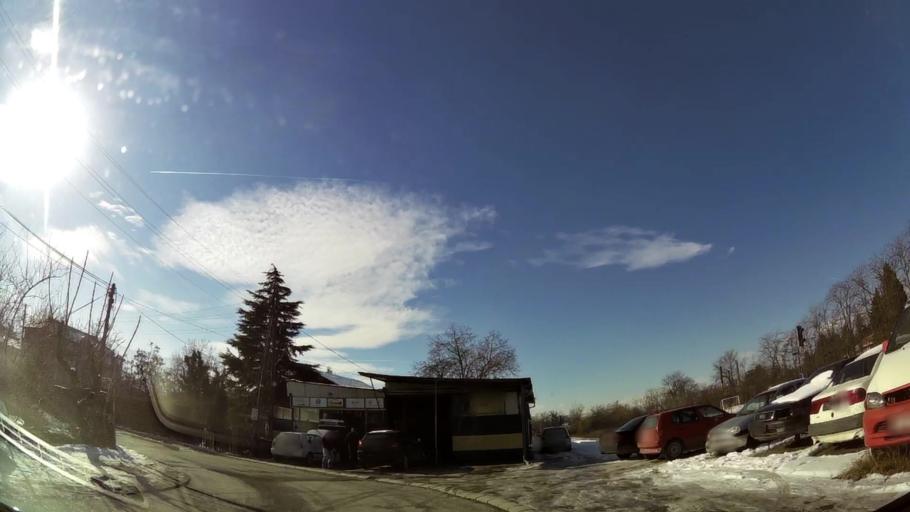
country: MK
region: Saraj
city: Saraj
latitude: 42.0111
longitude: 21.3573
